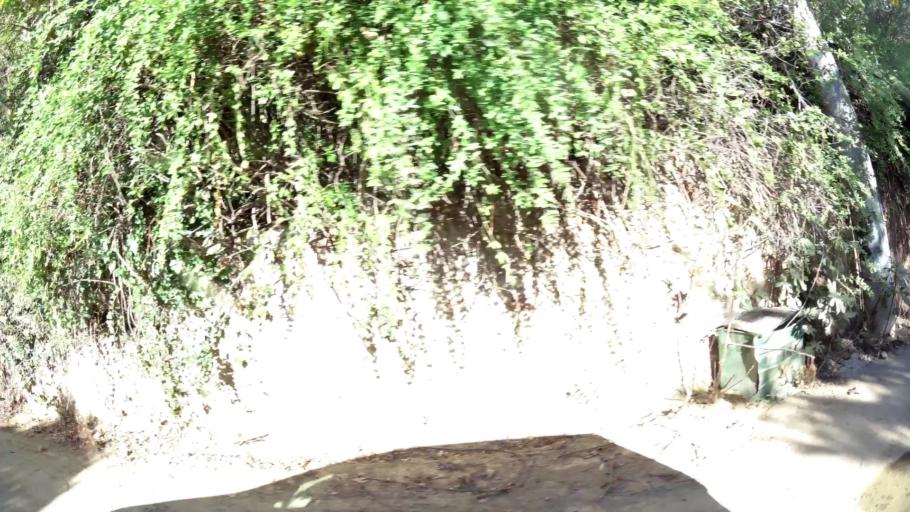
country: GR
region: Attica
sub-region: Nomarchia Anatolikis Attikis
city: Stamata
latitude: 38.1290
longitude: 23.8785
